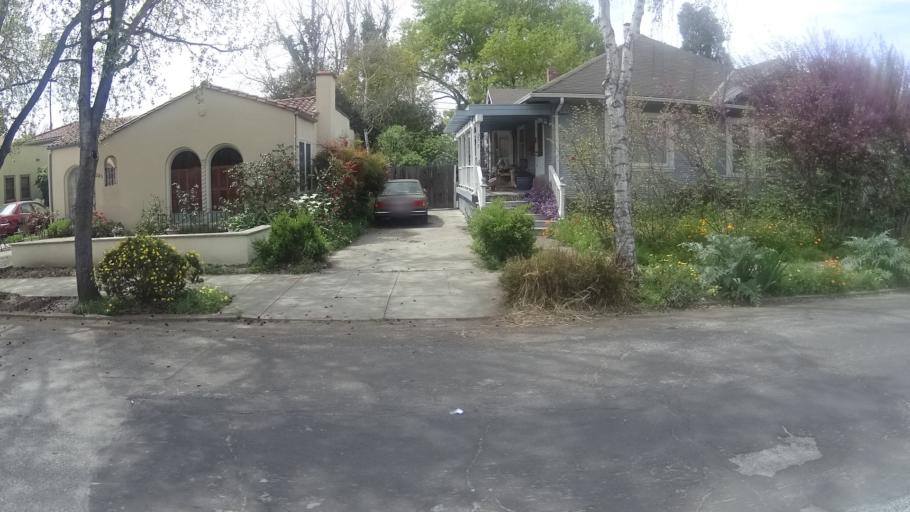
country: US
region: California
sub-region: Santa Clara County
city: San Jose
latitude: 37.3376
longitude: -121.8748
